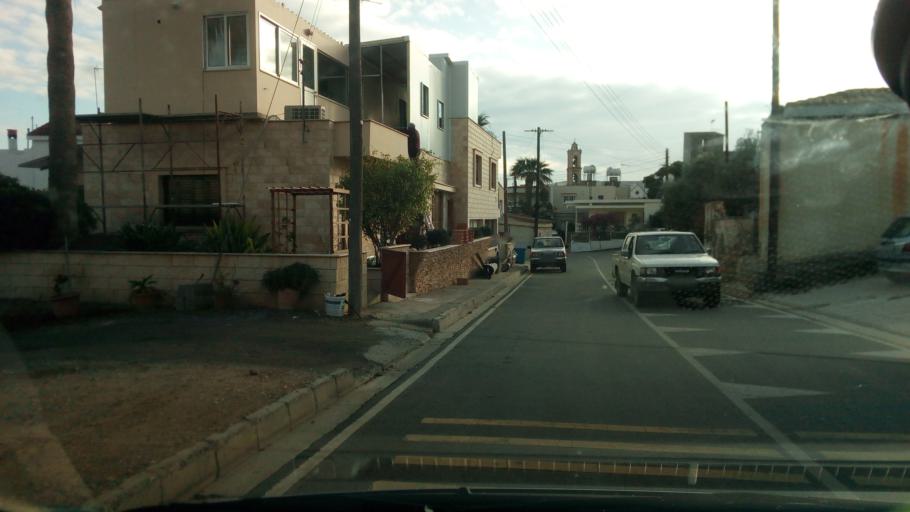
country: CY
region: Larnaka
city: Xylotymbou
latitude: 34.9927
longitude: 33.7821
